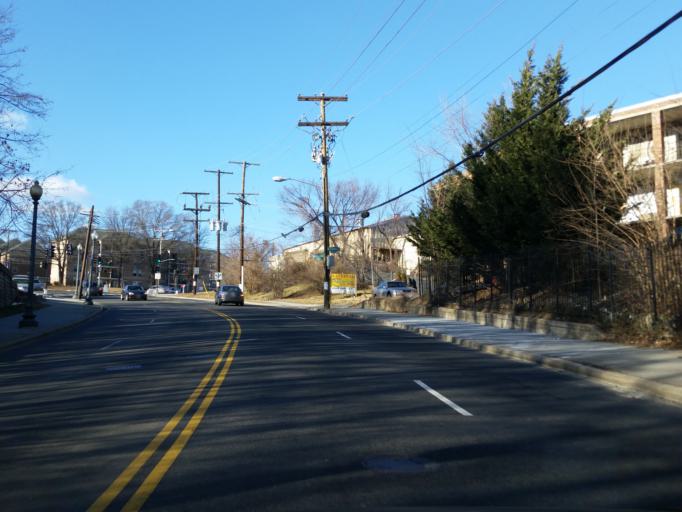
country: US
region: Maryland
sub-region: Prince George's County
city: Mount Rainier
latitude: 38.9190
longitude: -76.9784
